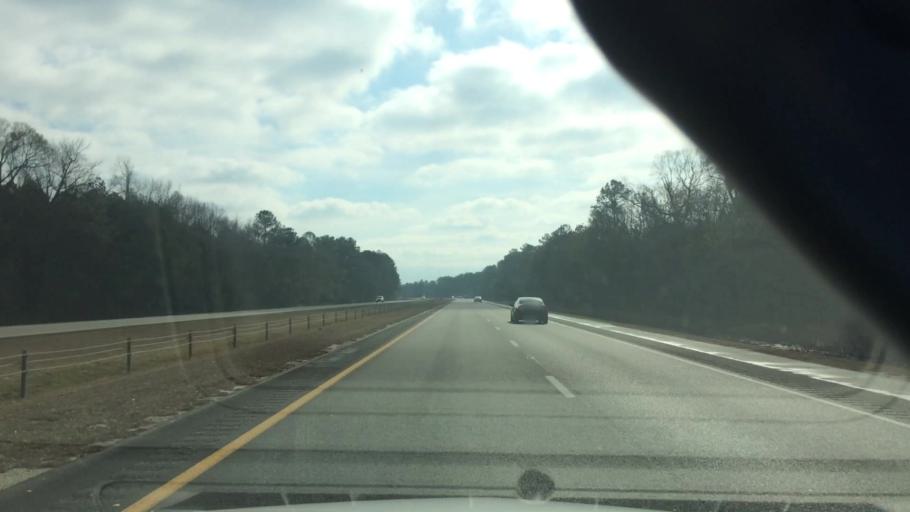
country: US
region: North Carolina
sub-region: Pender County
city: Burgaw
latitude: 34.5421
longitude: -77.8935
